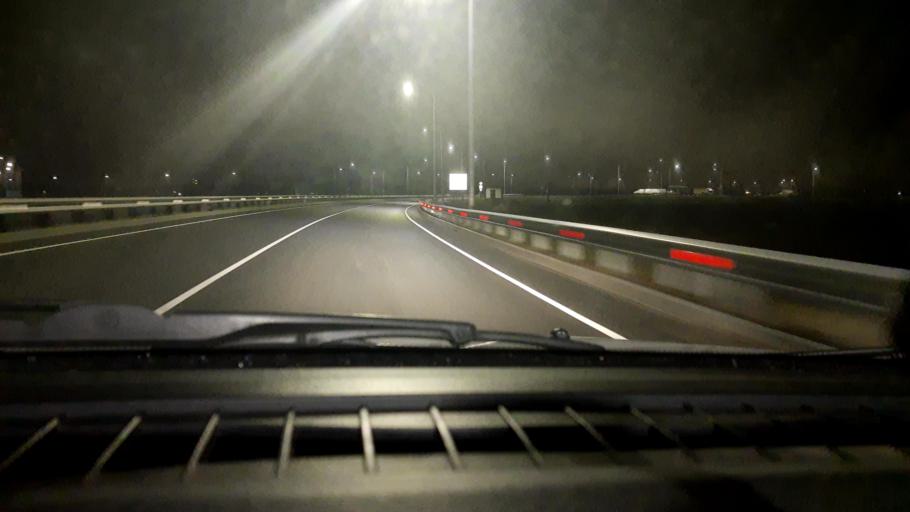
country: RU
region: Nizjnij Novgorod
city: Neklyudovo
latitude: 56.4251
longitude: 43.9915
